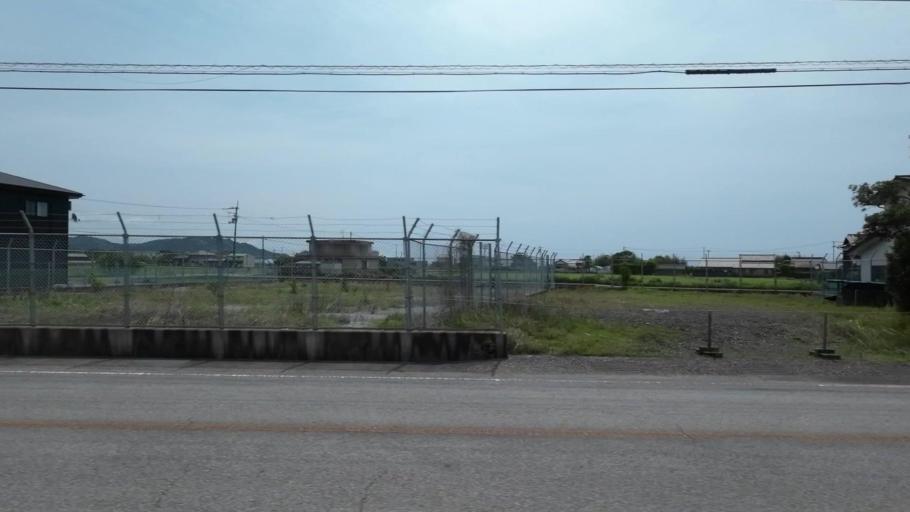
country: JP
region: Kochi
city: Kochi-shi
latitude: 33.5906
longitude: 133.6610
